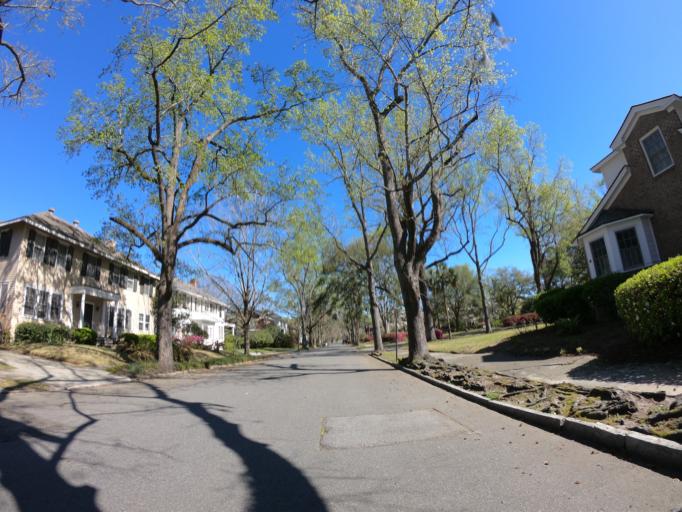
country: US
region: Georgia
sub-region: Chatham County
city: Savannah
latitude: 32.0464
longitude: -81.1037
